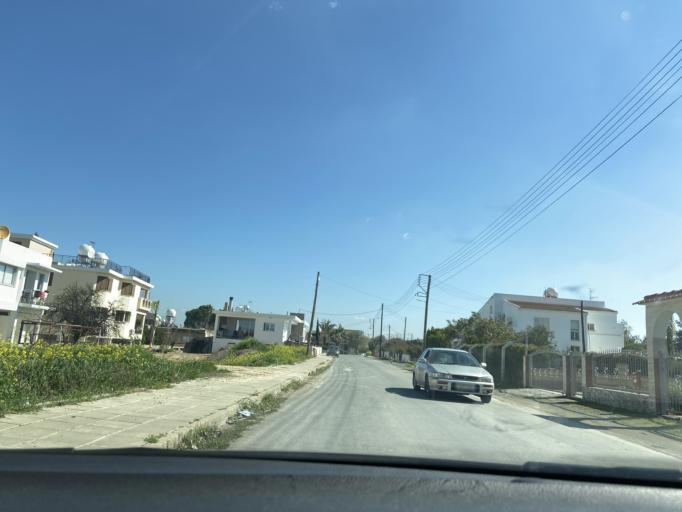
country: CY
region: Lefkosia
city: Dali
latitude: 35.0168
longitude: 33.4082
